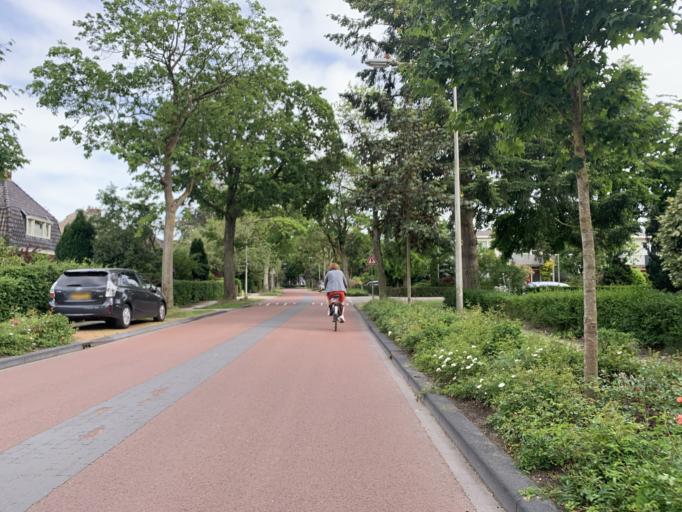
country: NL
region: Groningen
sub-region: Gemeente Haren
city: Haren
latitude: 53.1702
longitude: 6.6123
